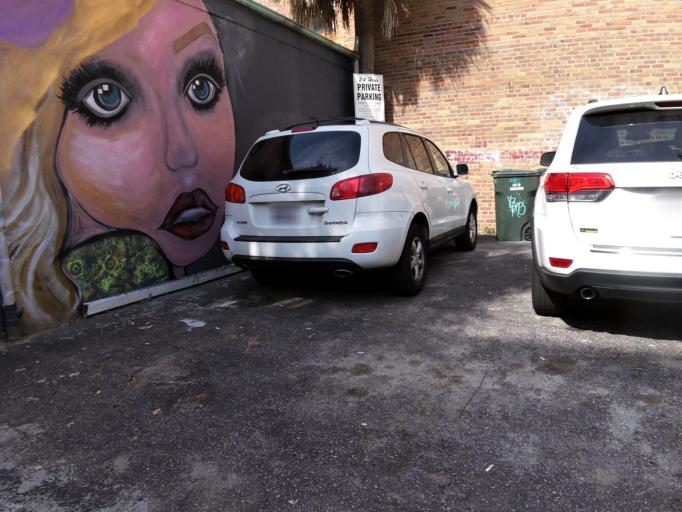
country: US
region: South Carolina
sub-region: Charleston County
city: Charleston
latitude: 32.7832
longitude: -79.9350
